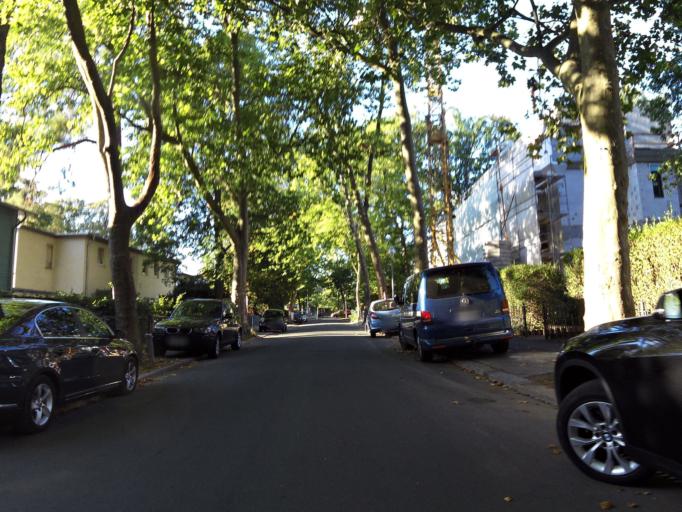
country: DE
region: Berlin
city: Grunewald
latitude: 52.4861
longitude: 13.2611
